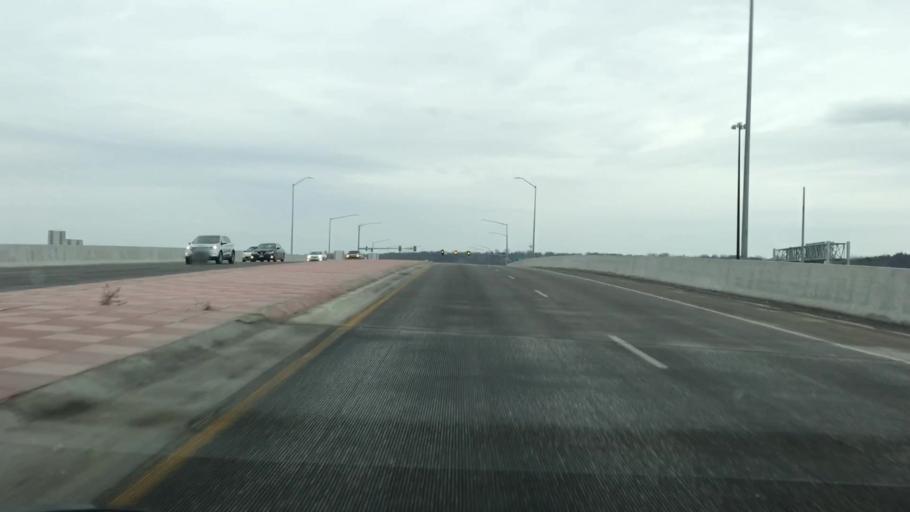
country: US
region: Iowa
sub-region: Pottawattamie County
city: Council Bluffs
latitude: 41.2199
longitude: -95.8332
